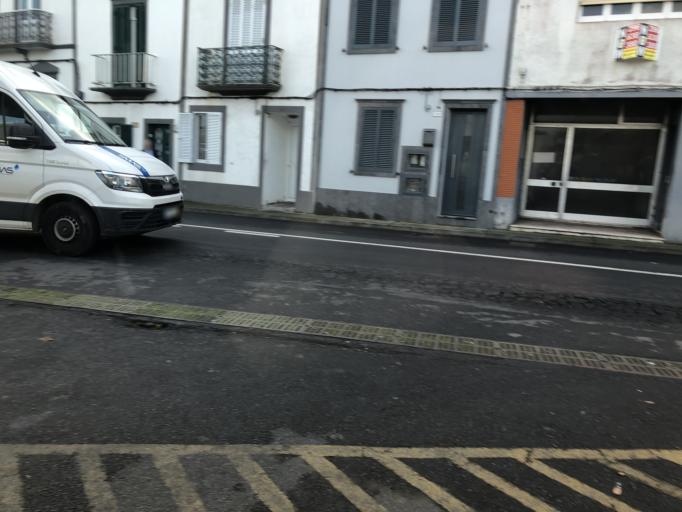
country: PT
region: Azores
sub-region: Ponta Delgada
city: Rosto de Cao
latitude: 37.7431
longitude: -25.6517
